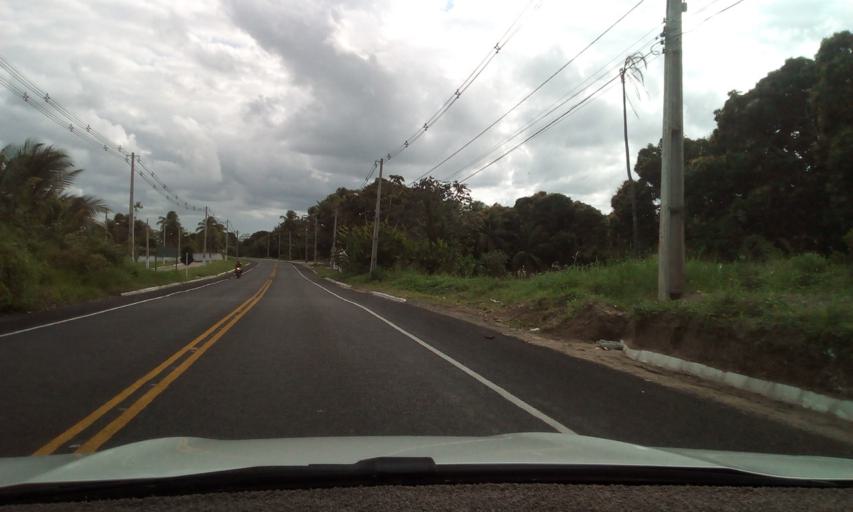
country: BR
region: Paraiba
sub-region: Rio Tinto
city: Rio Tinto
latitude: -6.8130
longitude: -35.0906
